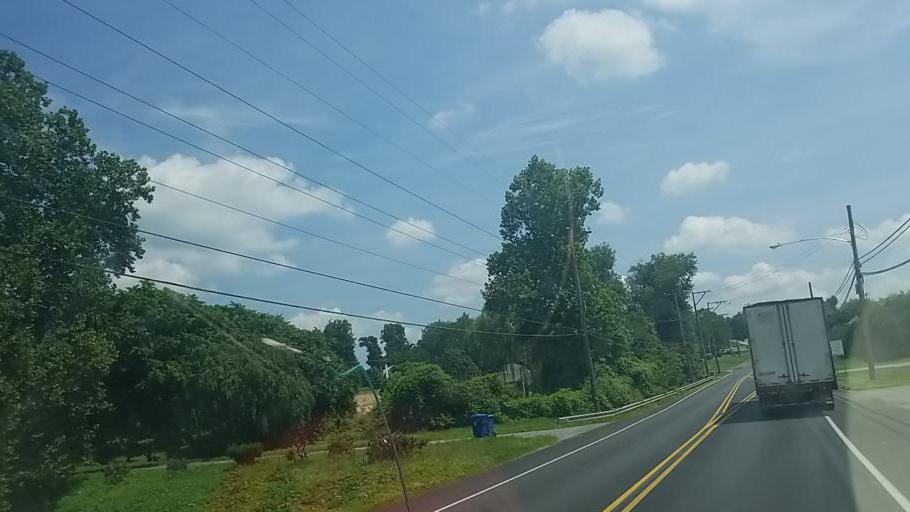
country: US
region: Pennsylvania
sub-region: Chester County
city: Toughkenamon
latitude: 39.8106
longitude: -75.7545
